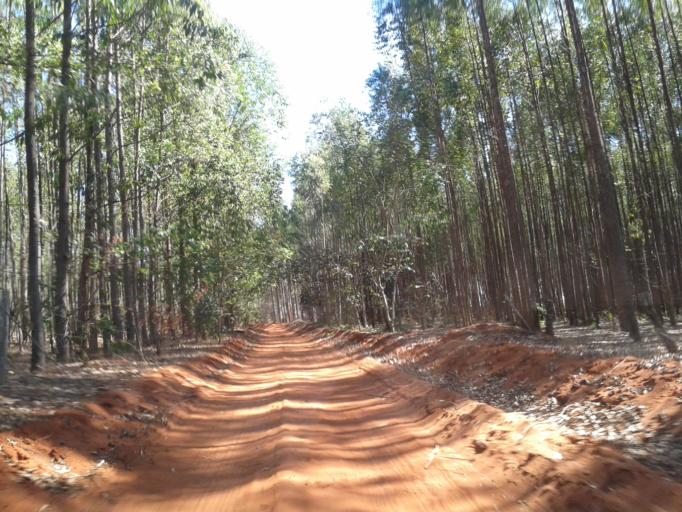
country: BR
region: Minas Gerais
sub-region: Ituiutaba
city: Ituiutaba
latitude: -19.0128
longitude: -49.2197
